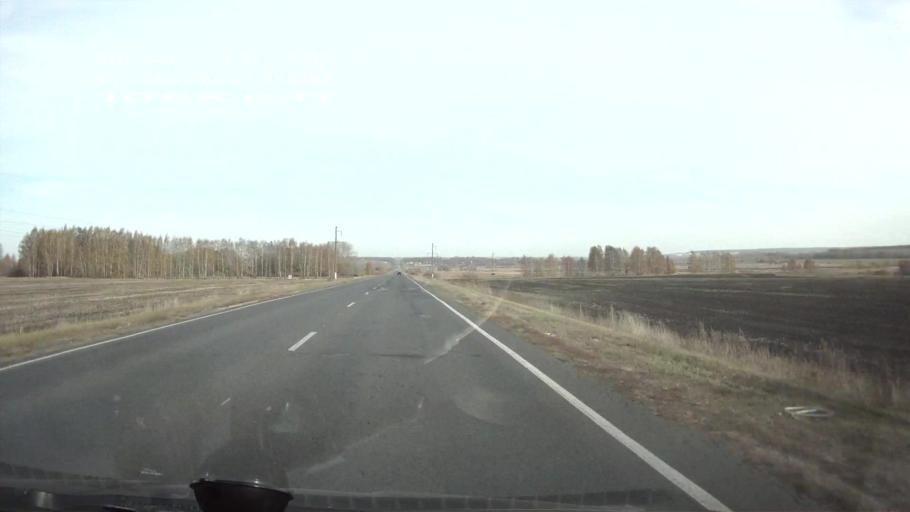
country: RU
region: Mordoviya
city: Atyashevo
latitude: 54.5435
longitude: 45.9406
